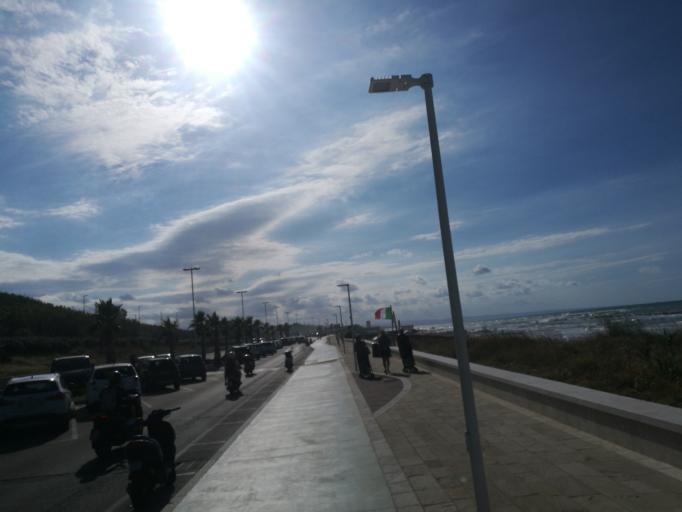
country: IT
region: Molise
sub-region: Provincia di Campobasso
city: Termoli
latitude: 42.0068
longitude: 14.9762
